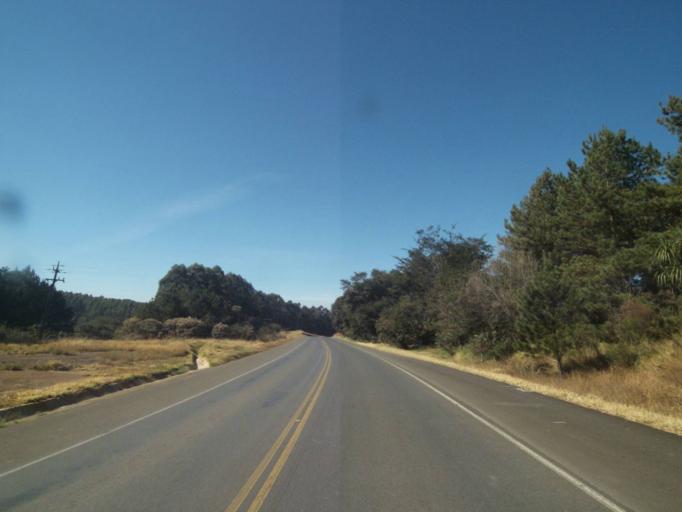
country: BR
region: Parana
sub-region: Tibagi
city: Tibagi
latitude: -24.5111
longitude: -50.4407
